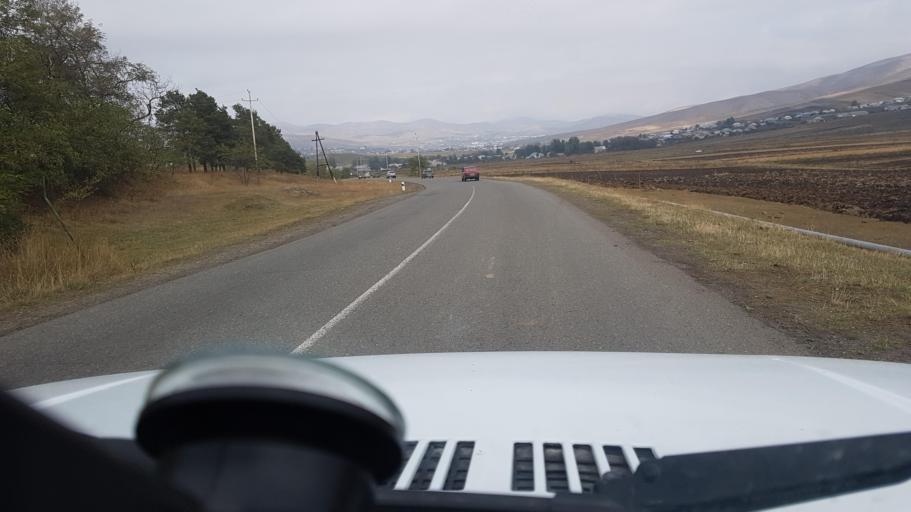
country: AZ
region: Gadabay Rayon
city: Ariqdam
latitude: 40.6242
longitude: 45.8164
